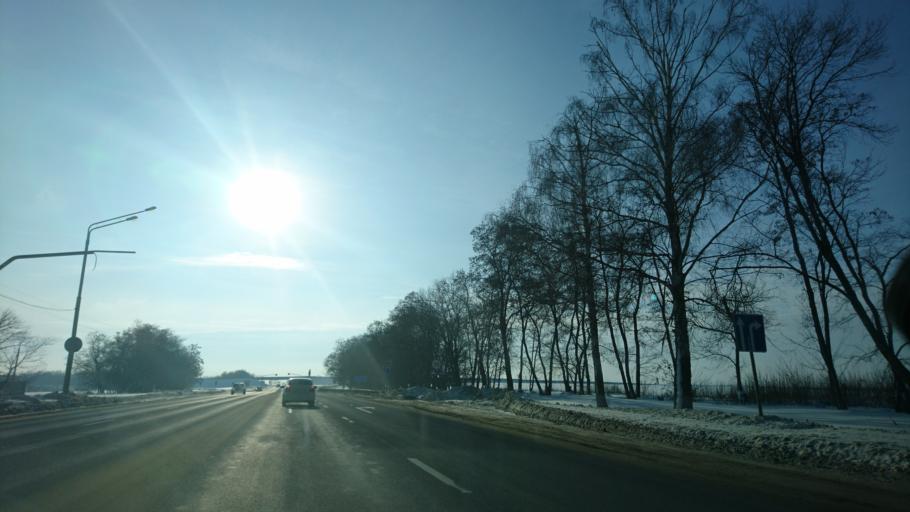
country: RU
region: Belgorod
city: Severnyy
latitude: 50.7286
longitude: 36.5295
